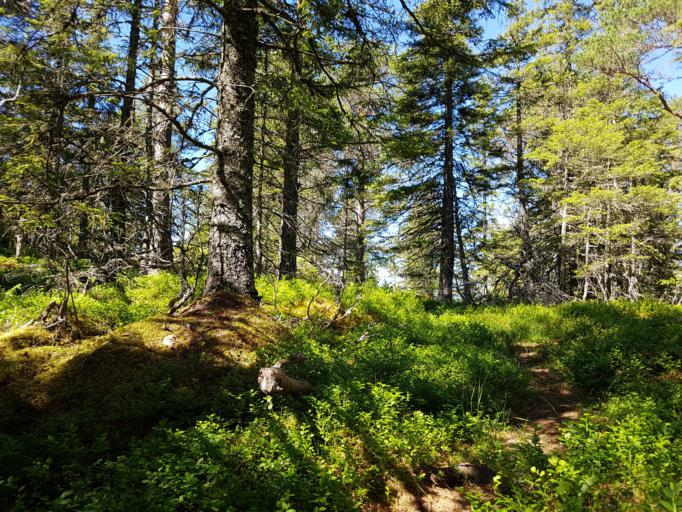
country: NO
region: Sor-Trondelag
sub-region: Melhus
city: Melhus
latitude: 63.4390
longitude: 10.2136
